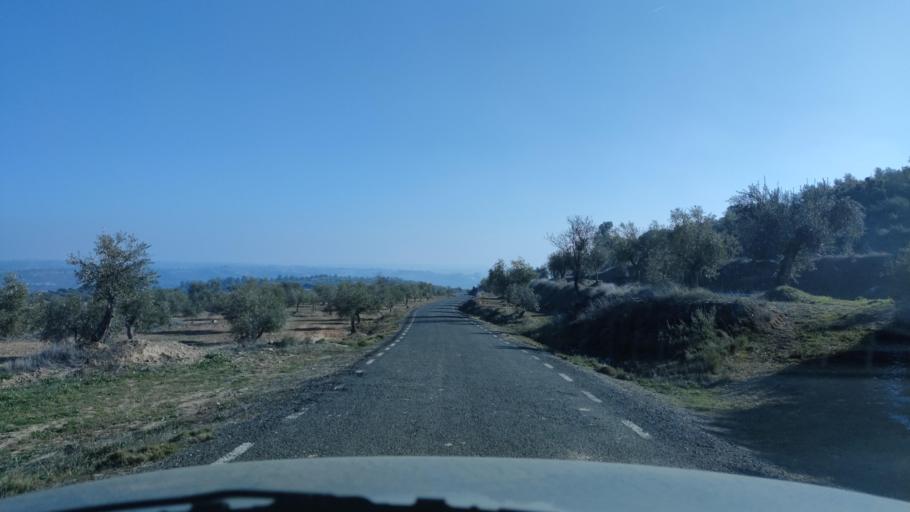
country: ES
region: Catalonia
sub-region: Provincia de Lleida
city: Torrebesses
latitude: 41.4350
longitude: 0.5703
